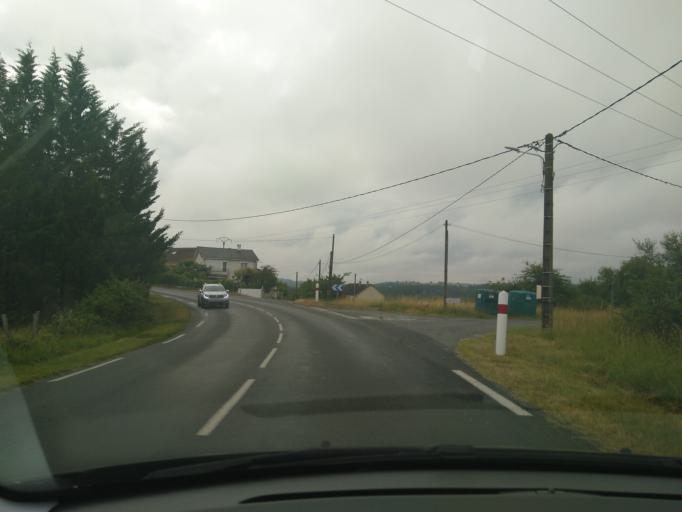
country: FR
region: Limousin
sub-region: Departement de la Correze
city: Brive-la-Gaillarde
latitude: 45.1033
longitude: 1.5355
